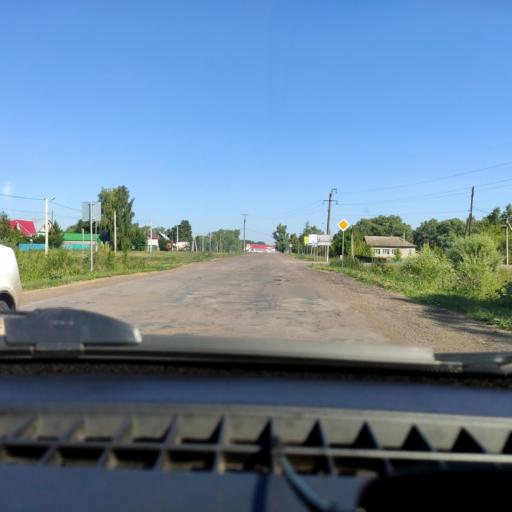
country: RU
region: Bashkortostan
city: Karmaskaly
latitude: 54.4050
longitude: 56.1629
